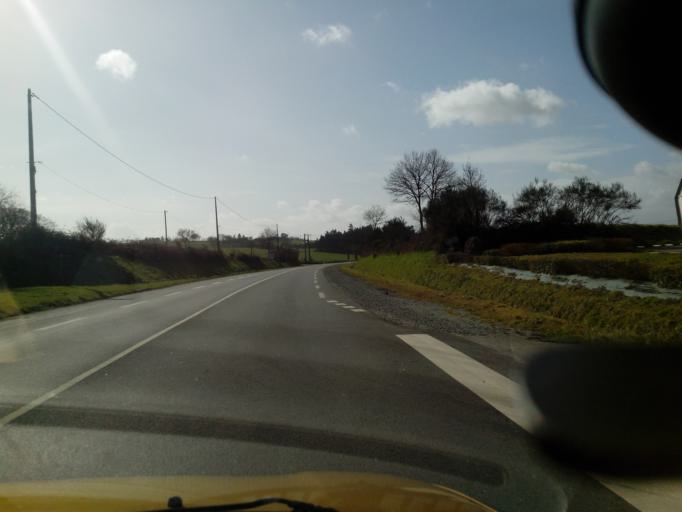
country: FR
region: Brittany
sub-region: Departement du Morbihan
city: Mauron
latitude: 48.0775
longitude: -2.2721
